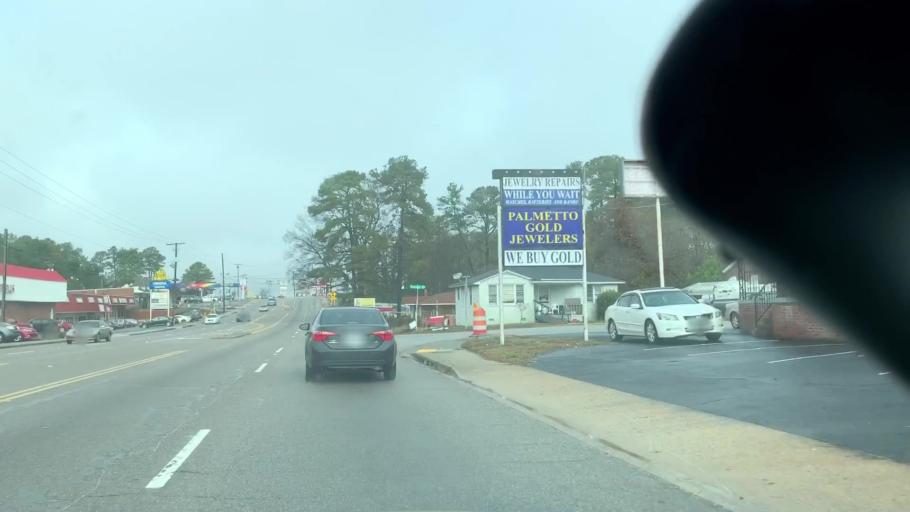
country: US
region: South Carolina
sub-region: Richland County
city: Woodfield
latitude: 34.0493
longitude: -80.9441
